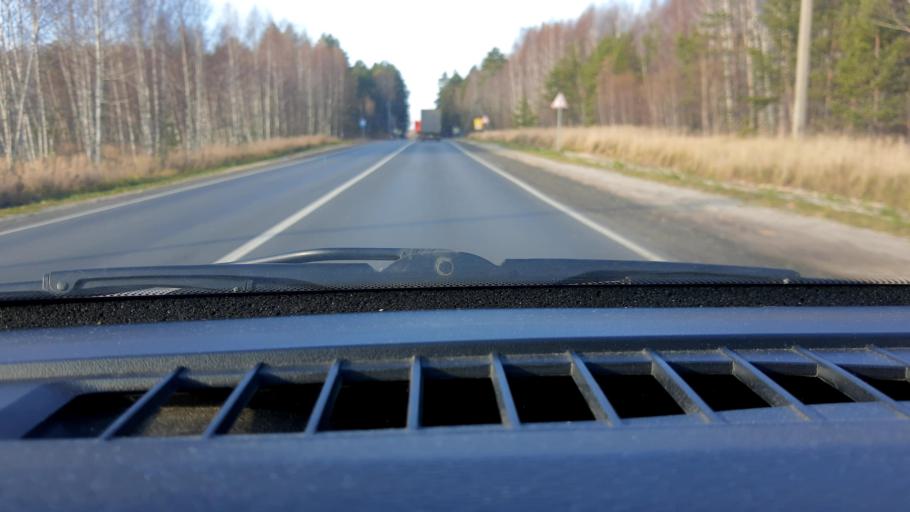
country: RU
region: Nizjnij Novgorod
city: Novaya Balakhna
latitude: 56.6130
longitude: 43.5927
